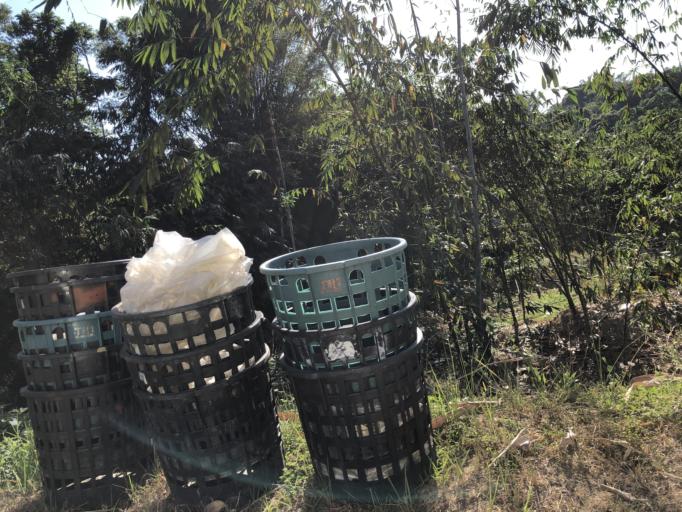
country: TW
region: Taiwan
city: Yujing
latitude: 23.0306
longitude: 120.3840
